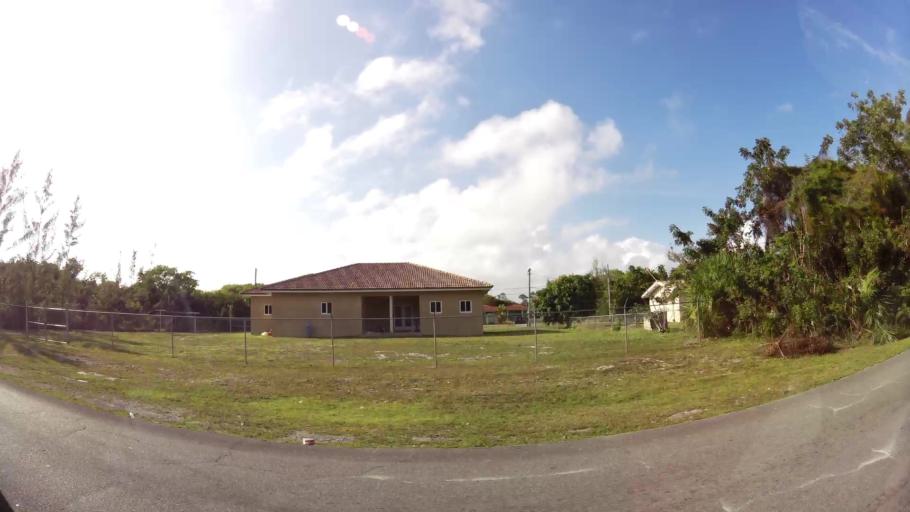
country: BS
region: Freeport
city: Lucaya
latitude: 26.5026
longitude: -78.6674
